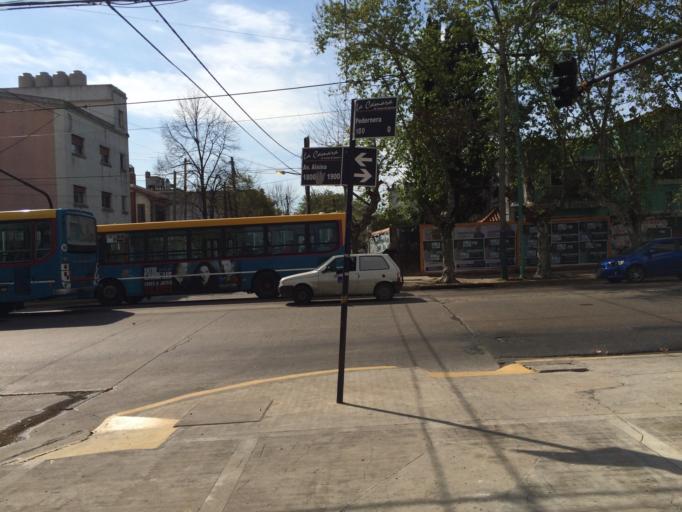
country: AR
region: Buenos Aires
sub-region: Partido de Lomas de Zamora
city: Lomas de Zamora
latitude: -34.7577
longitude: -58.3960
